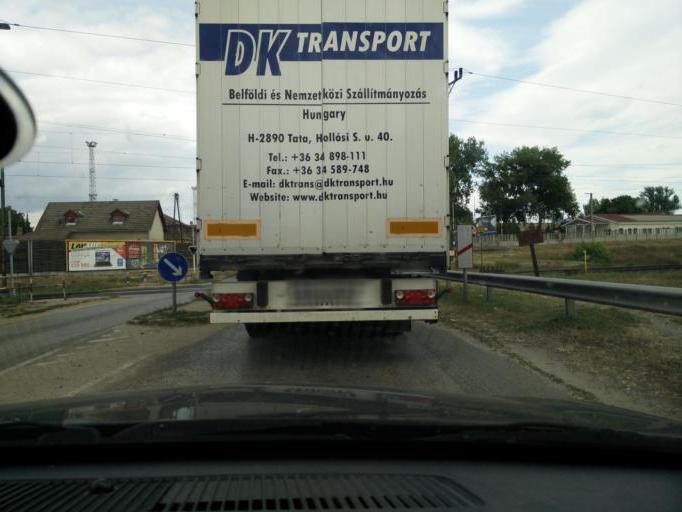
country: HU
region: Komarom-Esztergom
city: Tata
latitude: 47.6561
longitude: 18.3320
